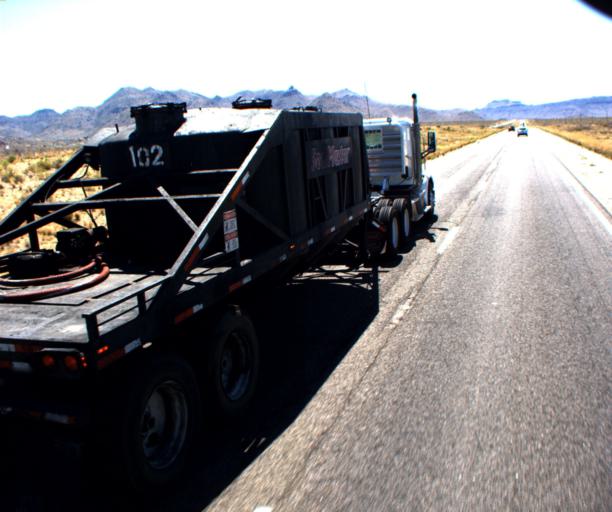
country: US
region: Arizona
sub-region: Mohave County
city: Golden Valley
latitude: 35.2709
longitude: -114.1684
